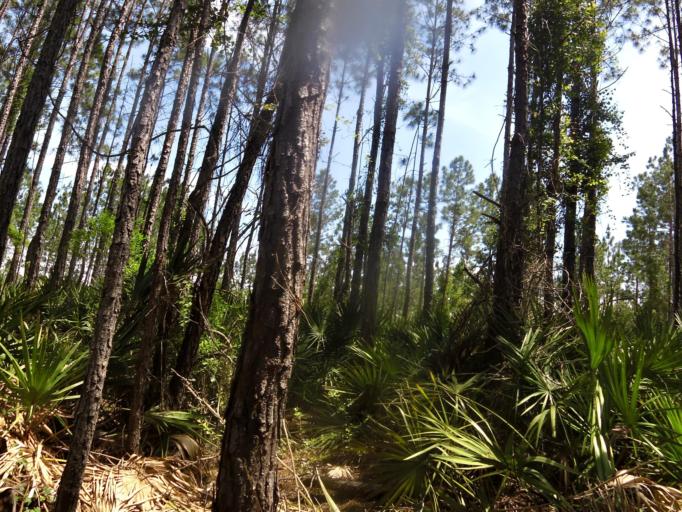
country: US
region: Florida
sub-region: Nassau County
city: Yulee
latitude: 30.4985
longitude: -81.4962
